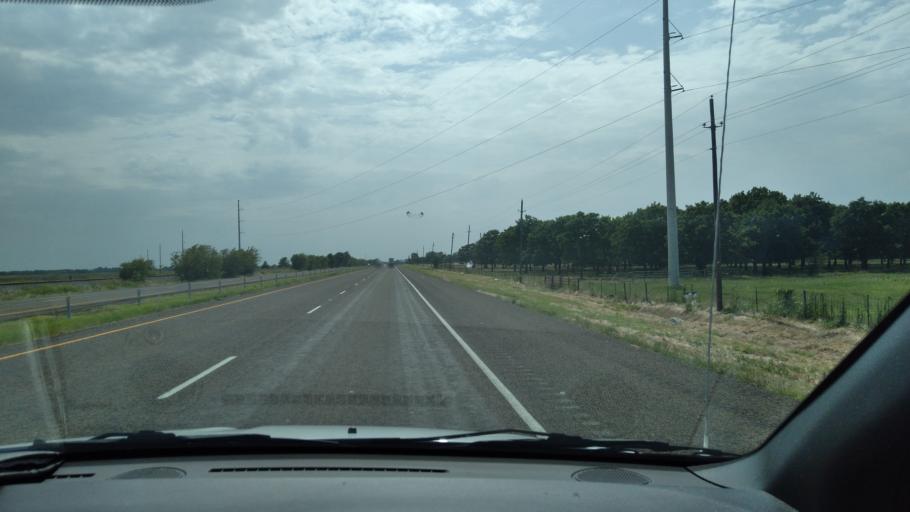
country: US
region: Texas
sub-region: Navarro County
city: Kerens
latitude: 32.1212
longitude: -96.3033
